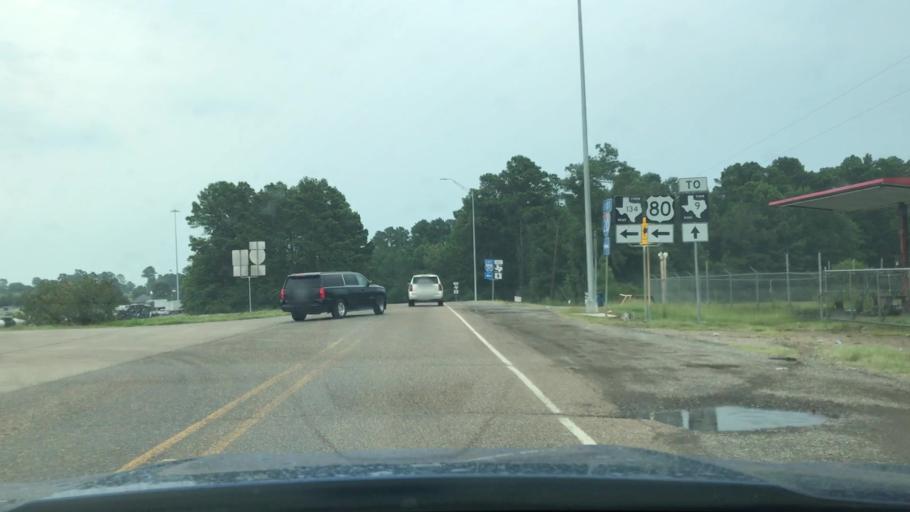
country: US
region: Texas
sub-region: Harrison County
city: Waskom
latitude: 32.4781
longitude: -94.0879
